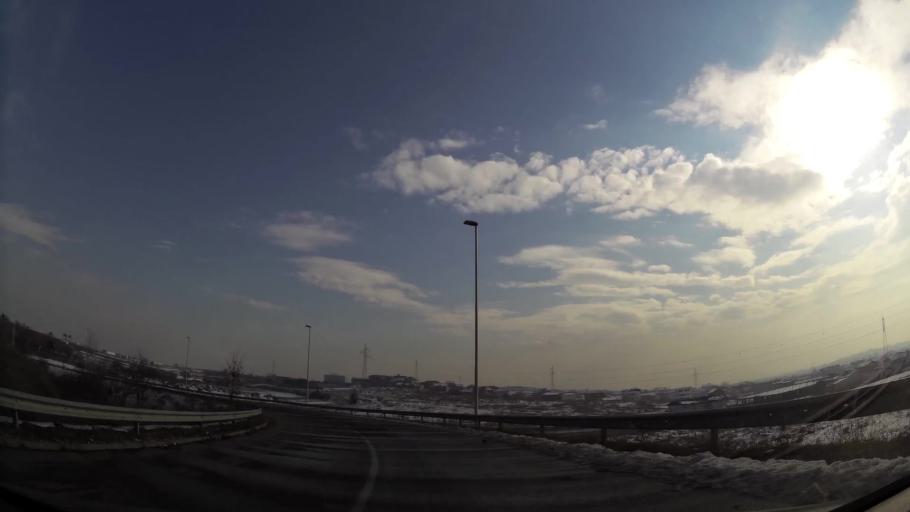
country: MK
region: Suto Orizari
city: Suto Orizare
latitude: 42.0515
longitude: 21.4210
